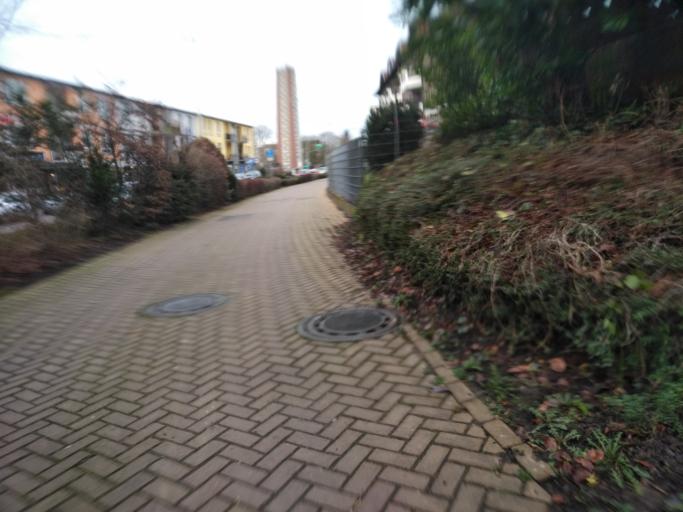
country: DE
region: North Rhine-Westphalia
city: Opladen
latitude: 51.0400
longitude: 7.0332
